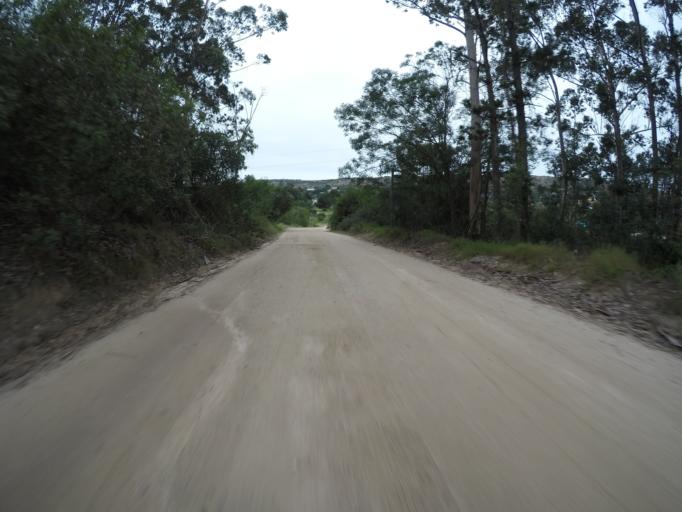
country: ZA
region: Western Cape
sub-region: Eden District Municipality
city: Knysna
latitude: -34.0167
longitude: 22.8151
